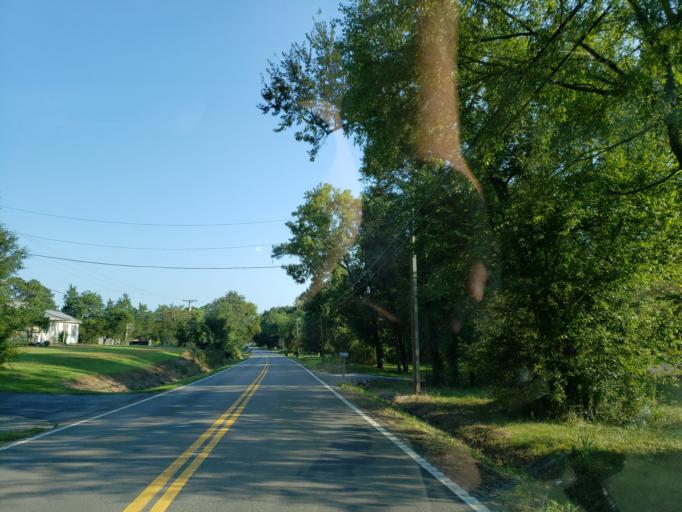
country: US
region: Tennessee
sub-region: Bradley County
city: Wildwood Lake
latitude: 35.0384
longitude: -84.8038
